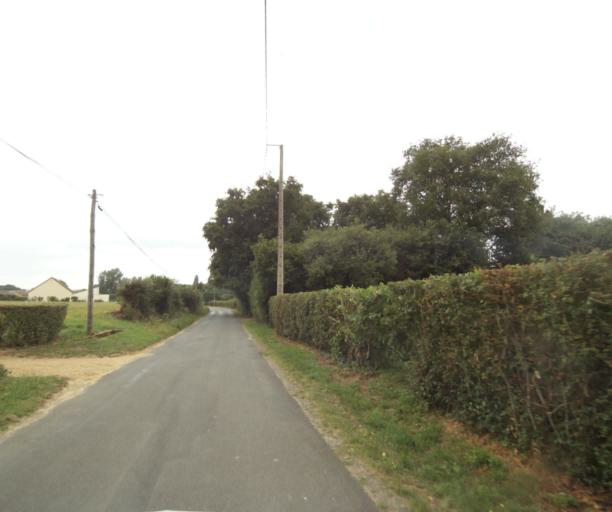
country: FR
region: Pays de la Loire
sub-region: Departement de la Sarthe
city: Juigne-sur-Sarthe
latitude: 47.8566
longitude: -0.2847
